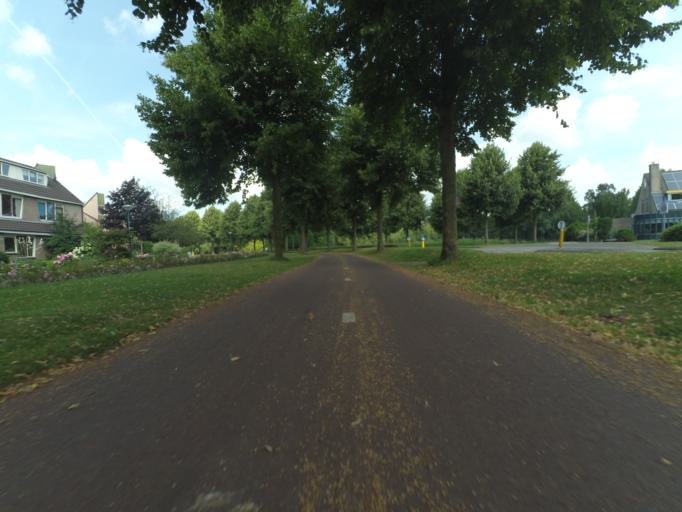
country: NL
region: Utrecht
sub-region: Gemeente Zeist
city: Zeist
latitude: 52.0561
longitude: 5.2391
